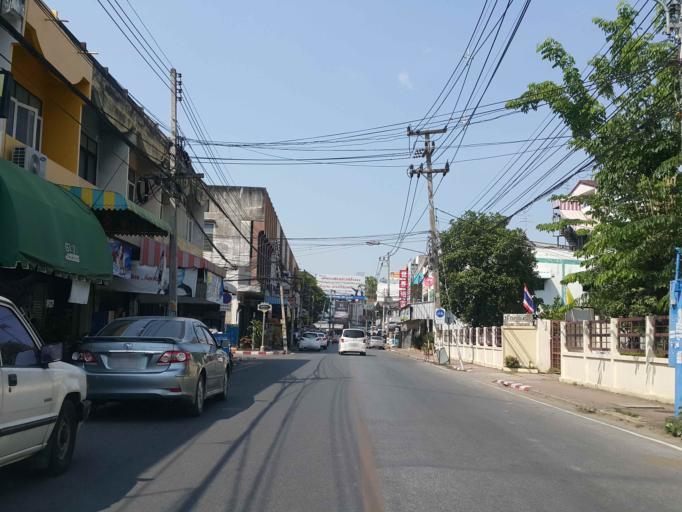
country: TH
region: Chiang Mai
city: Chiang Mai
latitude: 18.7739
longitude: 99.0008
